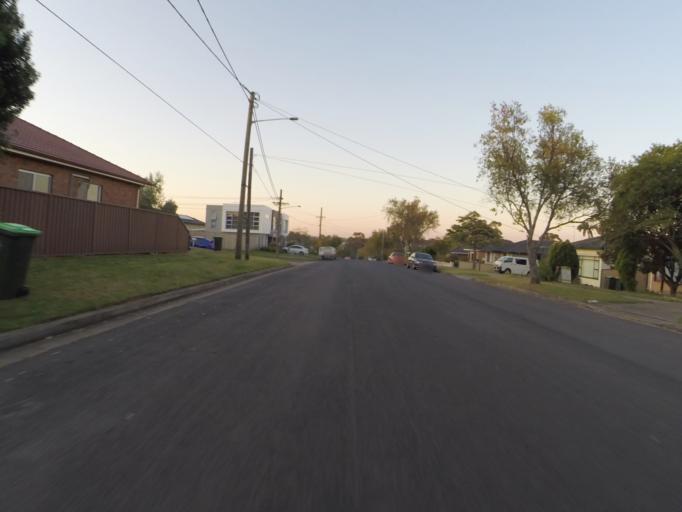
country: AU
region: New South Wales
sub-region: Bankstown
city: Revesby
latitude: -33.9680
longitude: 151.0122
